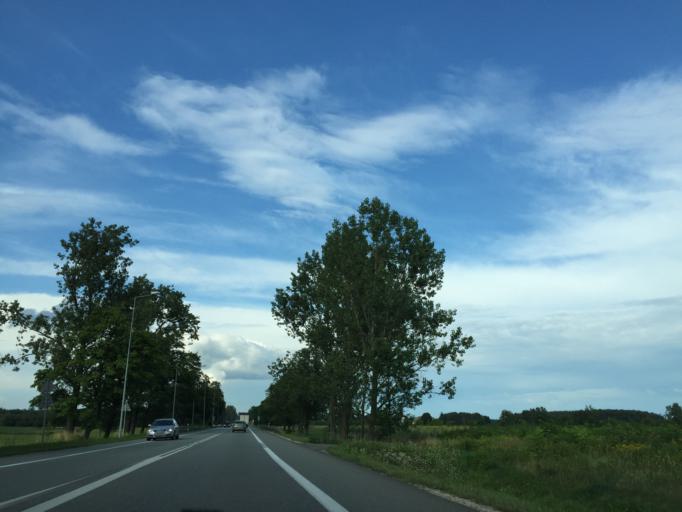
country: PL
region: Masovian Voivodeship
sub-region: Powiat otwocki
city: Karczew
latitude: 52.0190
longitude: 21.2942
